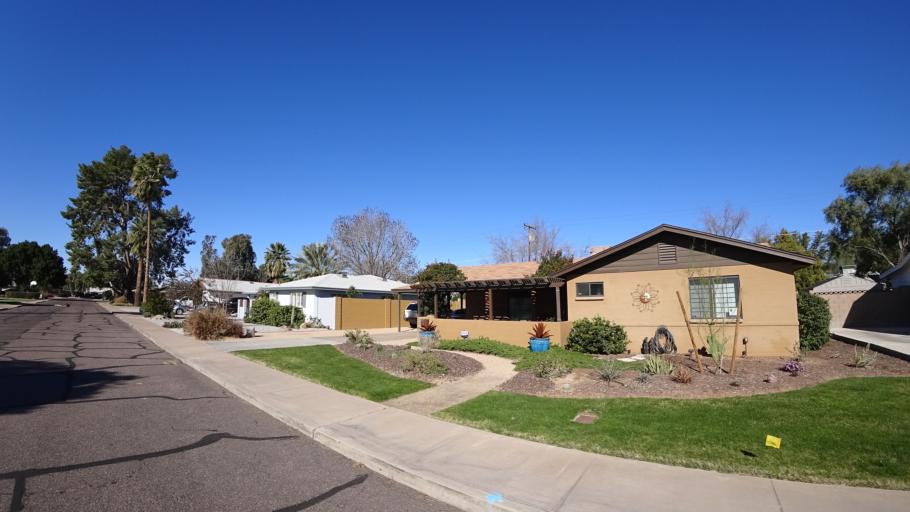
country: US
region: Arizona
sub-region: Maricopa County
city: Phoenix
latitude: 33.5034
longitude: -112.0406
